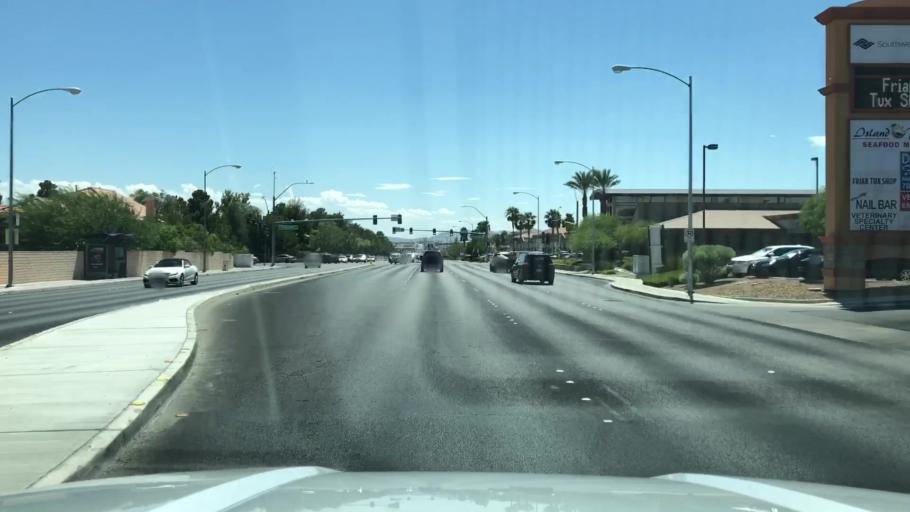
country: US
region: Nevada
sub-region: Clark County
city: Spring Valley
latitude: 36.1012
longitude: -115.2793
